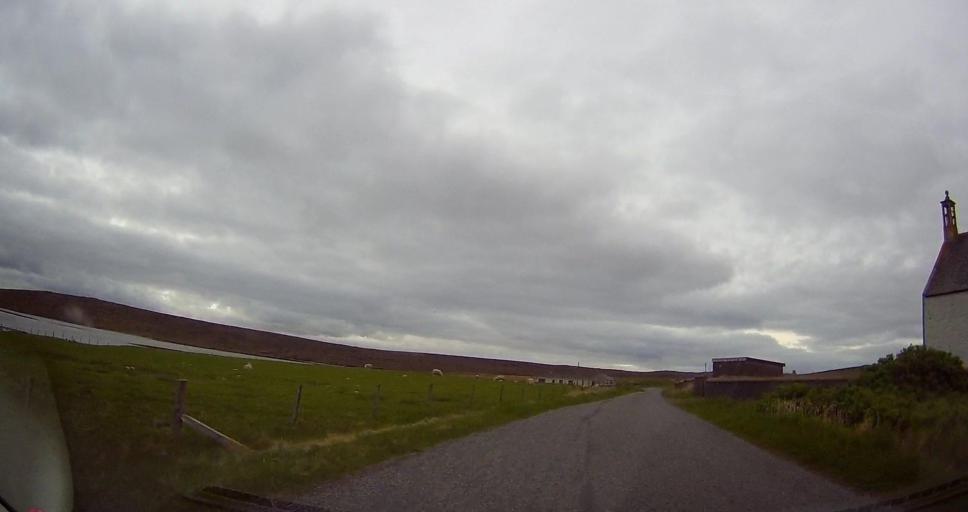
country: GB
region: Scotland
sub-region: Shetland Islands
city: Shetland
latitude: 60.5039
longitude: -1.1012
